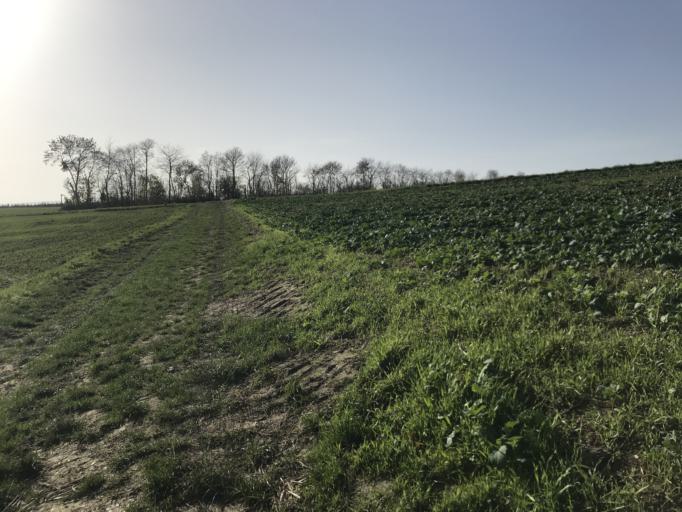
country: DE
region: Rheinland-Pfalz
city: Kaub
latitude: 50.0677
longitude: 7.7460
